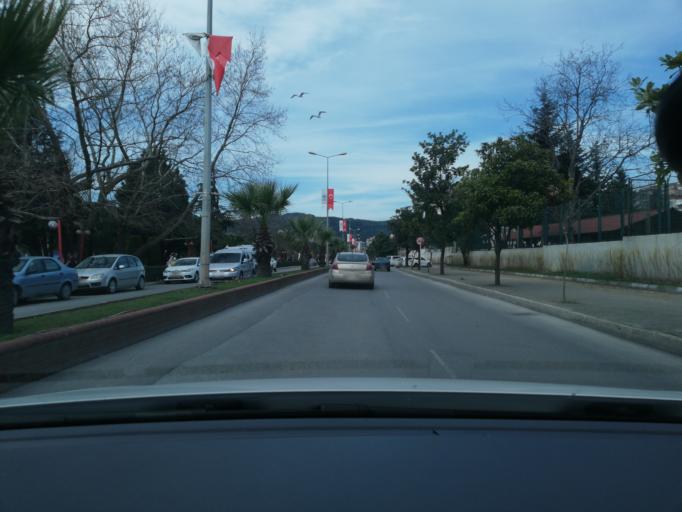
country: TR
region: Zonguldak
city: Eregli
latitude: 41.2853
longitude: 31.4125
